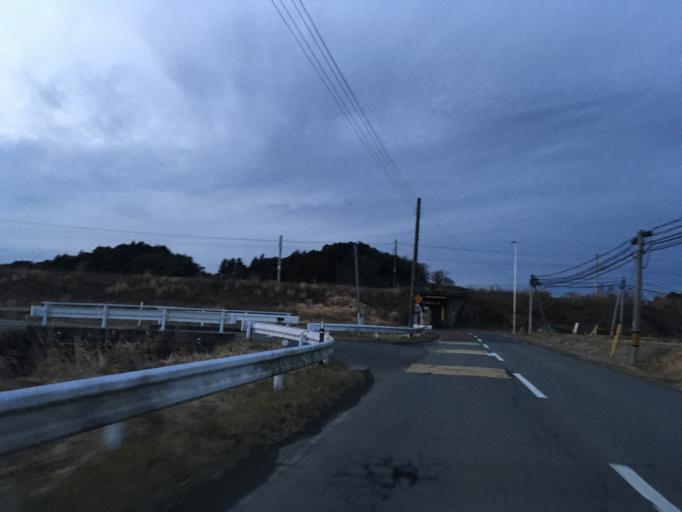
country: JP
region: Miyagi
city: Kogota
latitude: 38.6861
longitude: 141.0946
